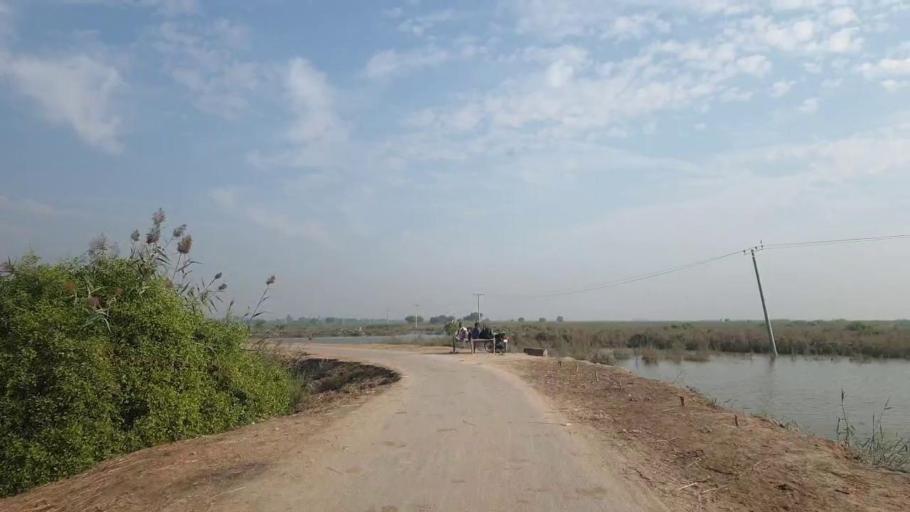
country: PK
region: Sindh
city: Tando Bago
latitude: 24.8569
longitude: 68.9660
